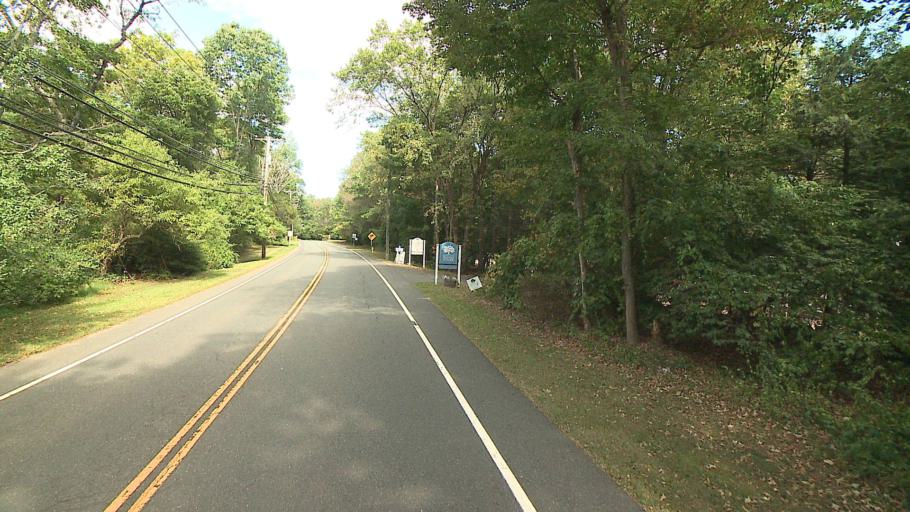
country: US
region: Connecticut
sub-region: Fairfield County
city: New Canaan
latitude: 41.1643
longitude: -73.4621
